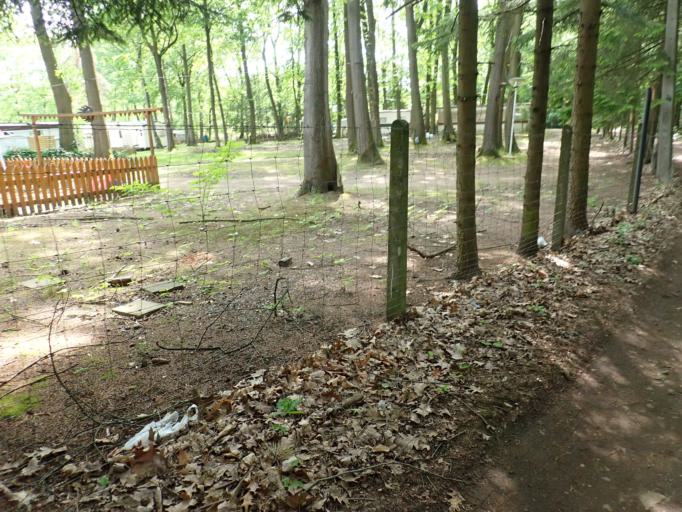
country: BE
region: Flanders
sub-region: Provincie Antwerpen
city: Herselt
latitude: 51.0625
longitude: 4.9048
